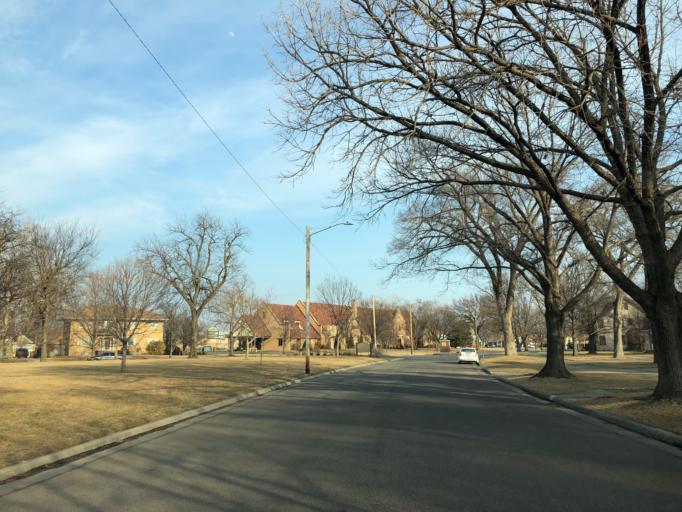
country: US
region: Kansas
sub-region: Reno County
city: Hutchinson
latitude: 38.0764
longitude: -97.9343
